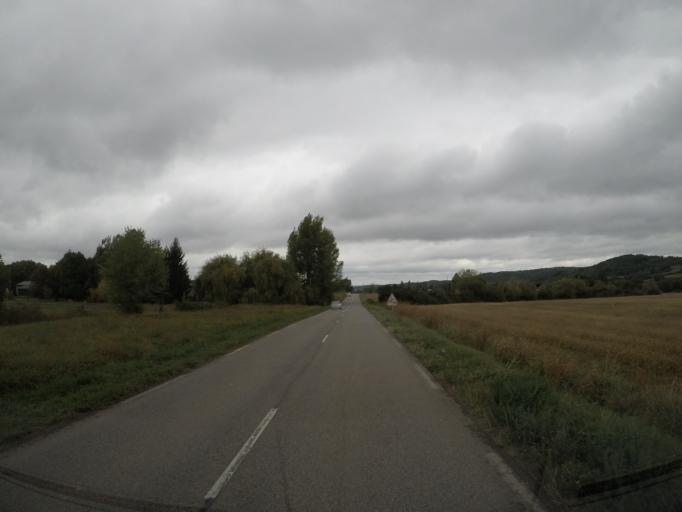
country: FR
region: Midi-Pyrenees
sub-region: Departement de la Haute-Garonne
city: Gaillac-Toulza
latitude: 43.1111
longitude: 1.4405
